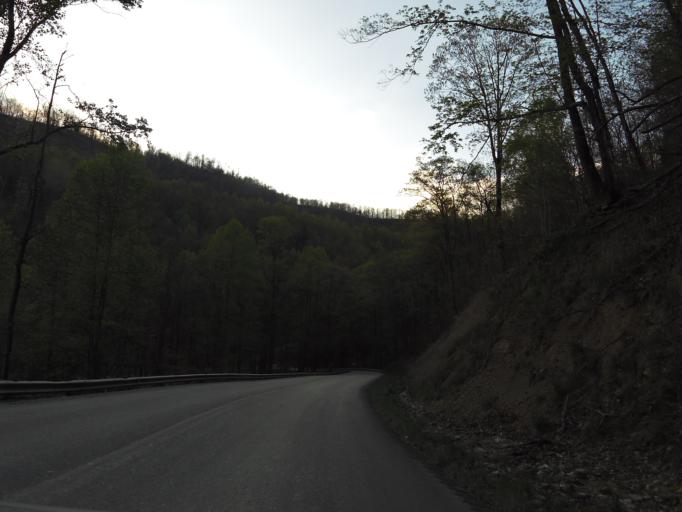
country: US
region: Kentucky
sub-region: Bell County
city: Middlesboro
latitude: 36.6232
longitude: -83.8776
